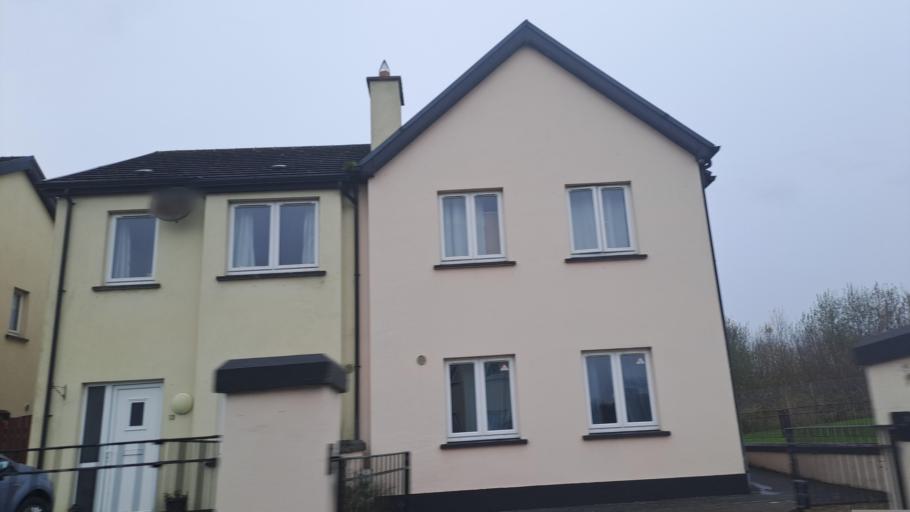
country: IE
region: Ulster
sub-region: An Cabhan
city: Virginia
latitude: 53.8371
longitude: -7.0710
